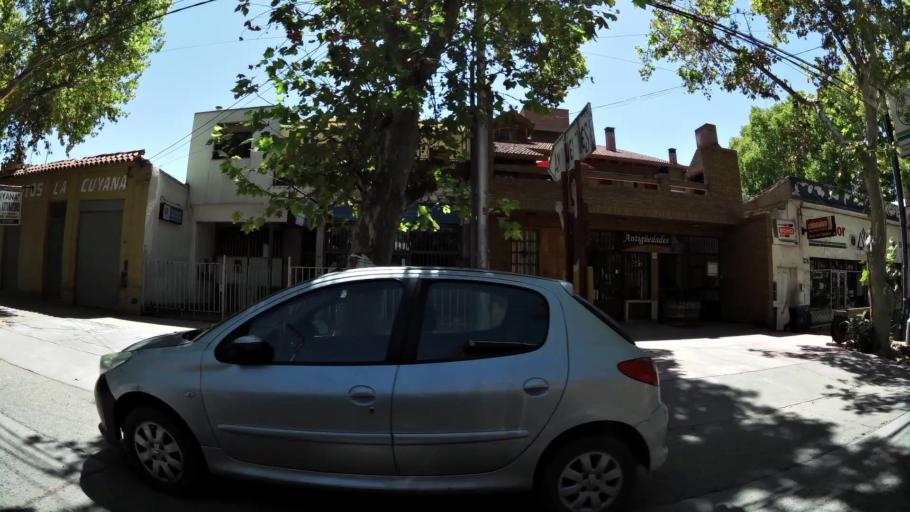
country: AR
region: Mendoza
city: Mendoza
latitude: -32.8941
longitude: -68.8257
